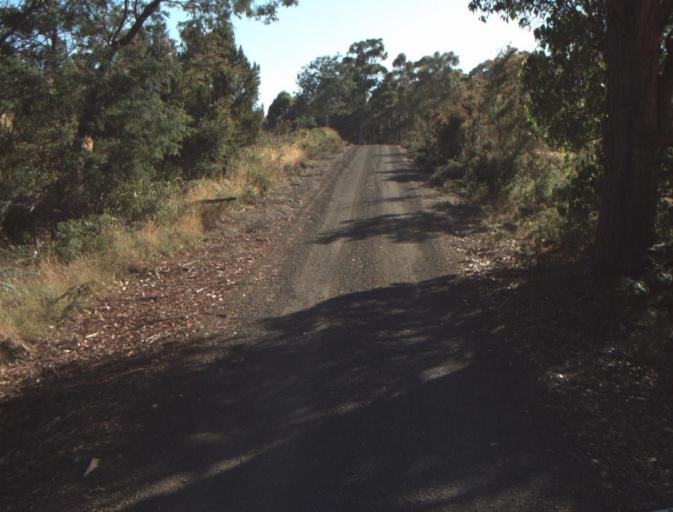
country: AU
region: Tasmania
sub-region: Launceston
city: Newstead
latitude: -41.4091
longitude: 147.2899
